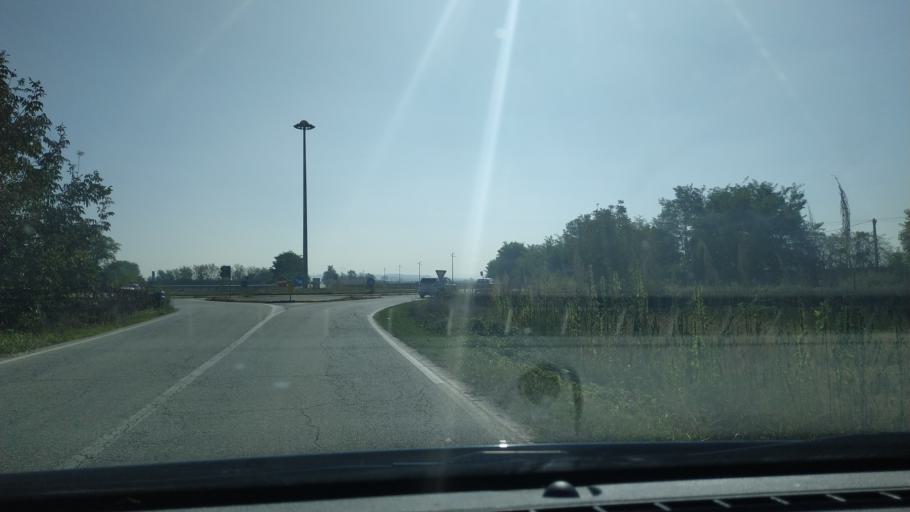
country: IT
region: Piedmont
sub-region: Provincia di Alessandria
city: Borgo San Martino
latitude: 45.0954
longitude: 8.5368
